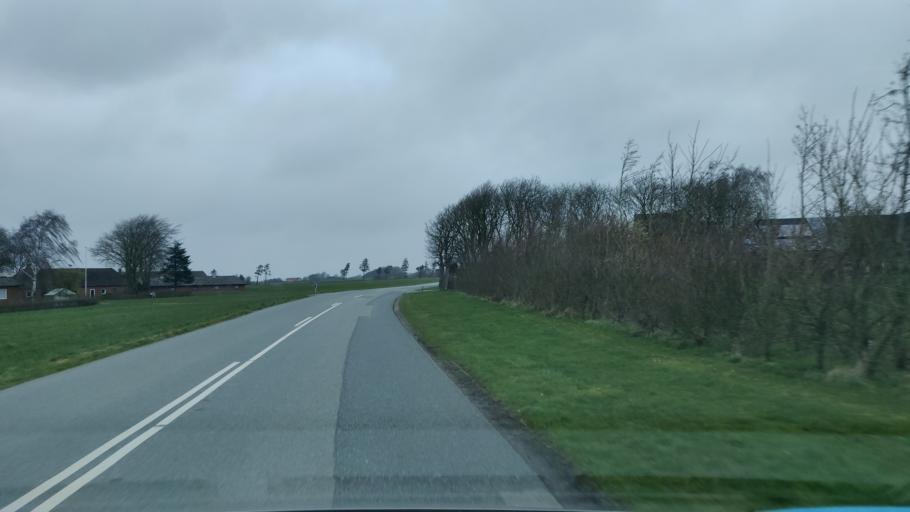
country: DK
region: Central Jutland
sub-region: Skive Kommune
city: Hojslev
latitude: 56.5788
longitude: 9.2288
